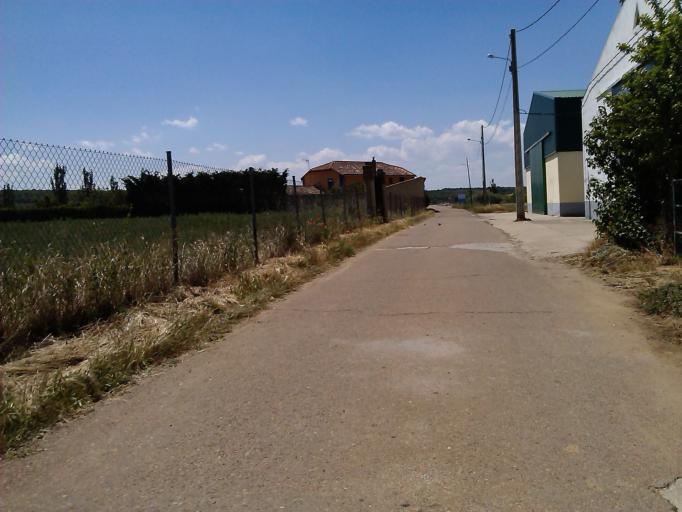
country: ES
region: Castille and Leon
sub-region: Provincia de Palencia
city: Cervatos de la Cueza
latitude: 42.3294
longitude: -4.8069
